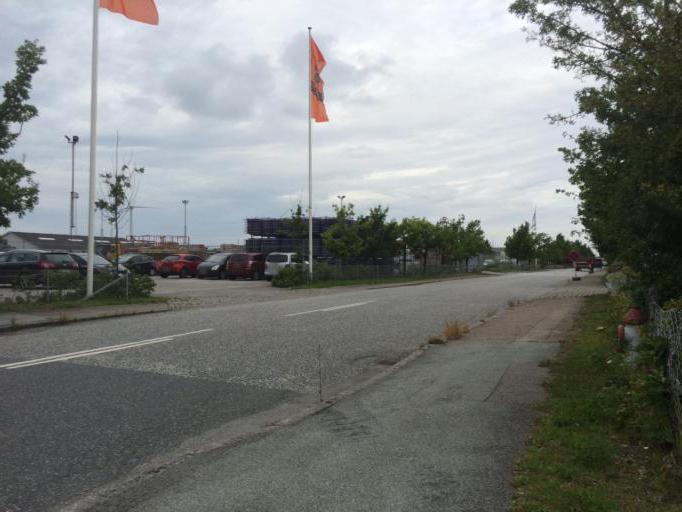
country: DK
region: Capital Region
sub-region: Hvidovre Kommune
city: Hvidovre
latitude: 55.6079
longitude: 12.4740
